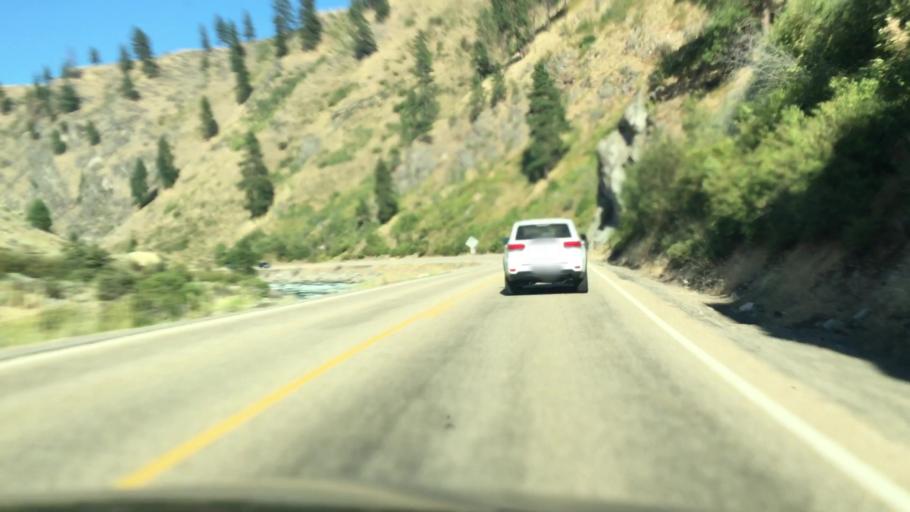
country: US
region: Idaho
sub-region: Boise County
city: Idaho City
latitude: 44.0892
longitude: -116.1096
